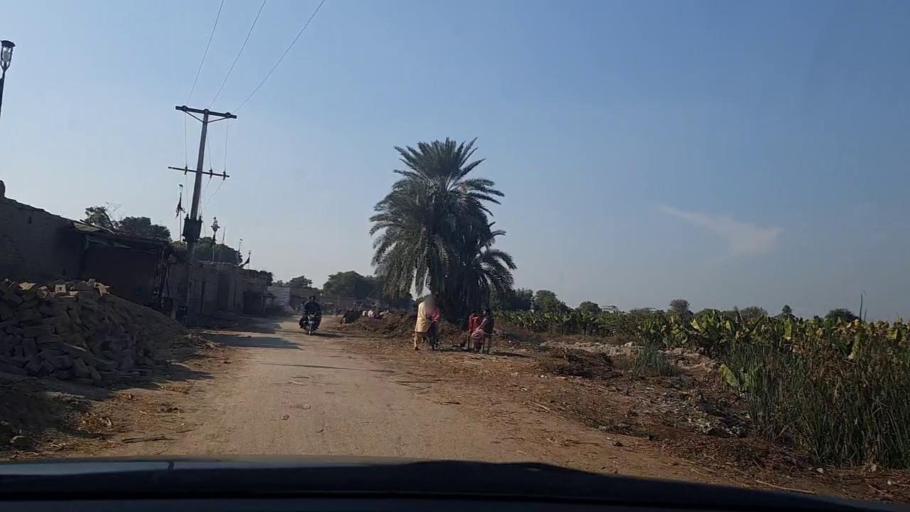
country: PK
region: Sindh
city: Daulatpur
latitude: 26.3049
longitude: 68.0892
